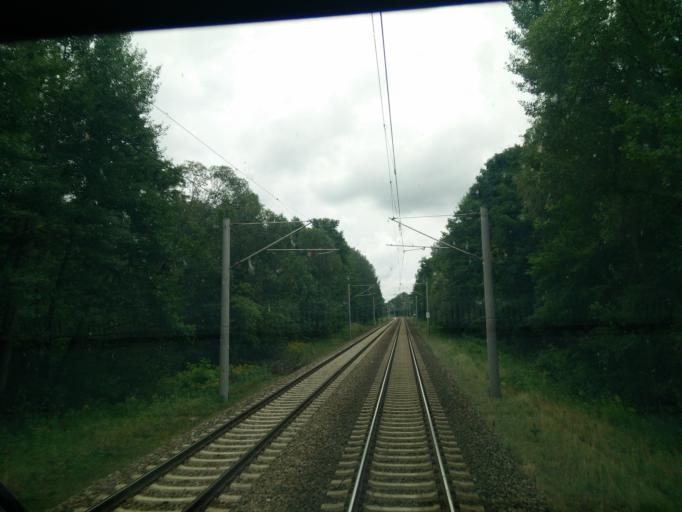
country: DE
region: Brandenburg
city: Schwerin
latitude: 52.1800
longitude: 13.6377
